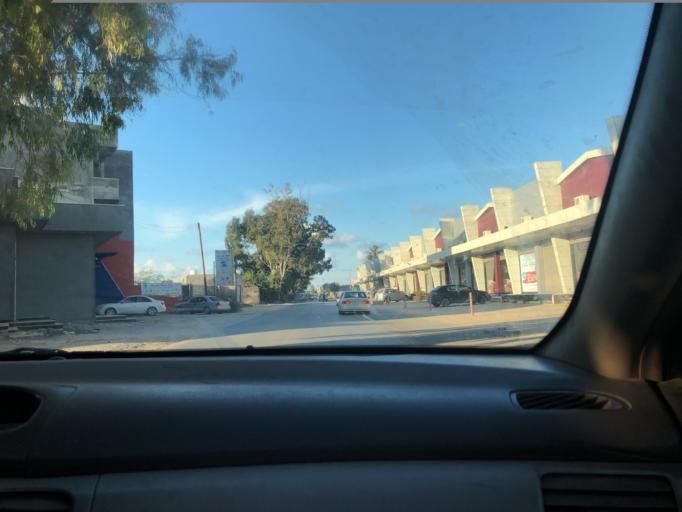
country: LY
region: Tripoli
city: Tagiura
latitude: 32.8603
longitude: 13.2787
